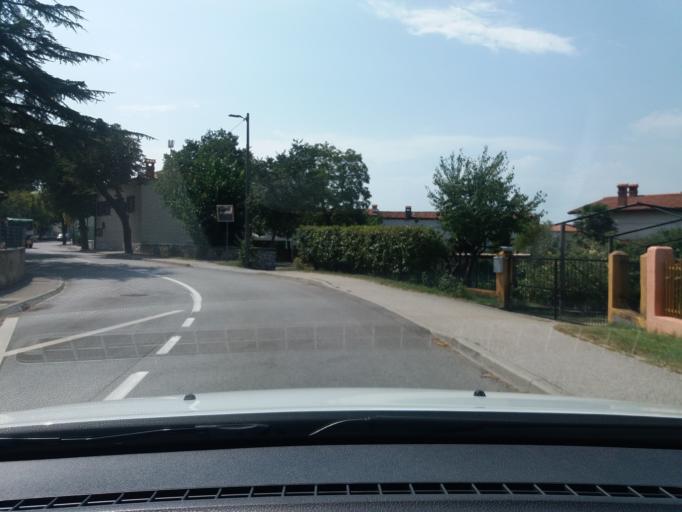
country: IT
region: Friuli Venezia Giulia
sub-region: Provincia di Gorizia
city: Doberdo del Lago
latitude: 45.8527
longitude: 13.5822
